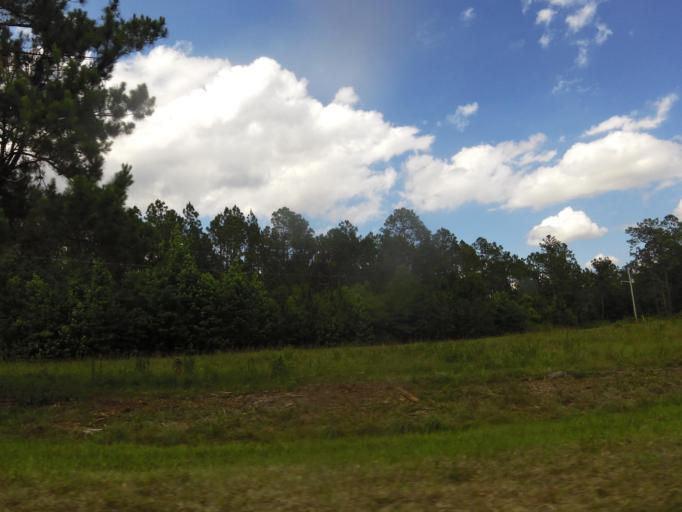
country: US
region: Florida
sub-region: Clay County
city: Asbury Lake
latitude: 29.9087
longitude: -81.8775
